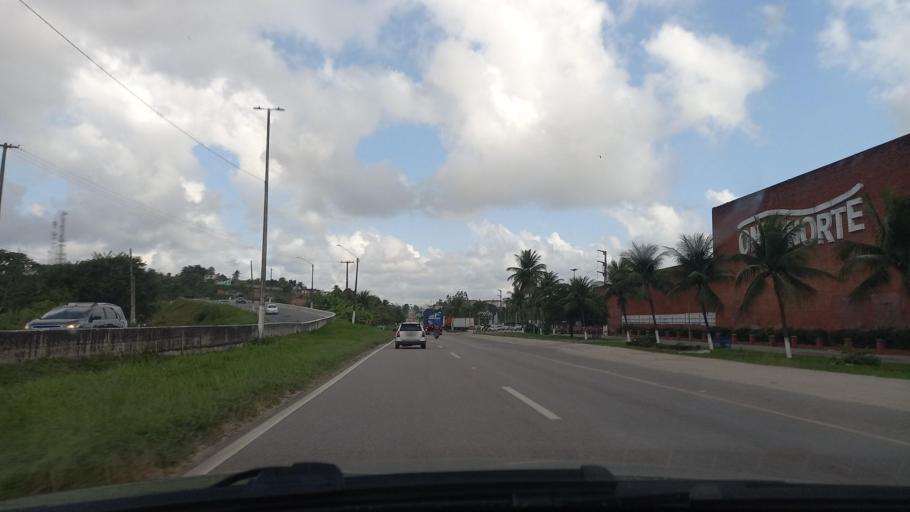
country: BR
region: Pernambuco
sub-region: Igarassu
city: Igarassu
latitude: -7.8317
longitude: -34.9142
